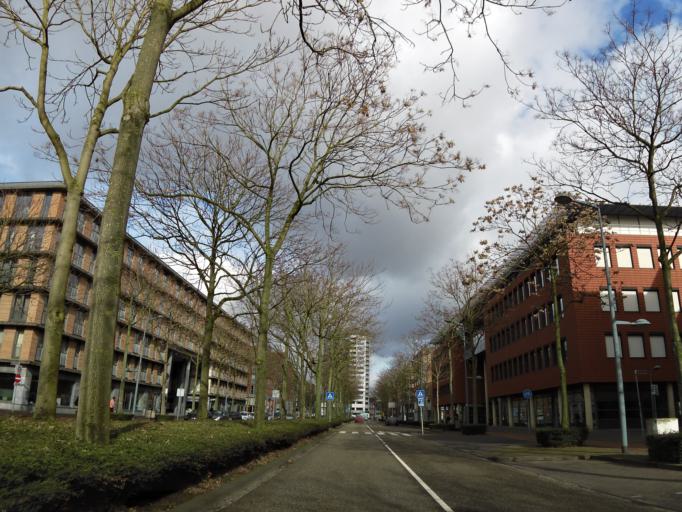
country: NL
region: Limburg
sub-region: Gemeente Maastricht
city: Maastricht
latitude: 50.8438
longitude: 5.7026
